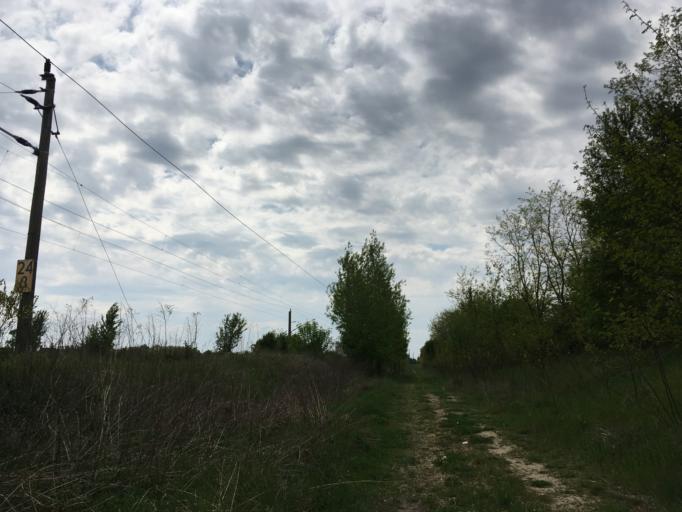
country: DE
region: Brandenburg
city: Bernau bei Berlin
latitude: 52.6925
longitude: 13.6105
